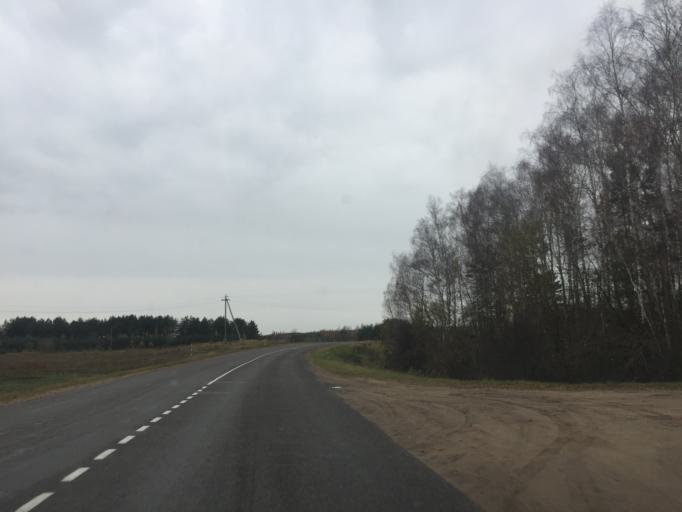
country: BY
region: Mogilev
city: Drybin
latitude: 54.1120
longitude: 31.1245
